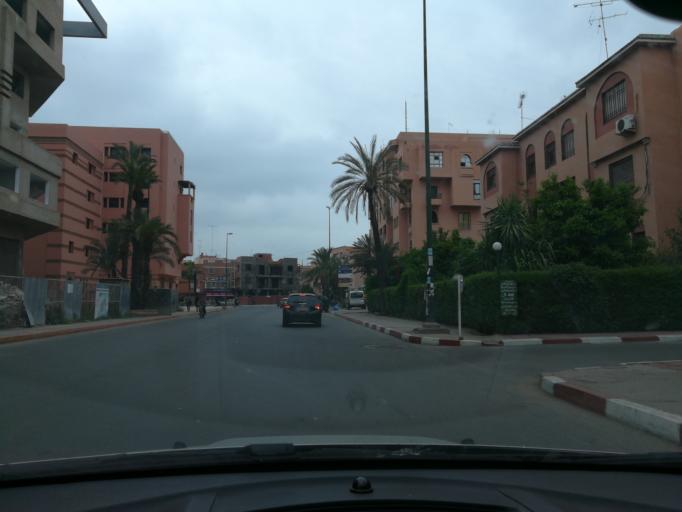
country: MA
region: Marrakech-Tensift-Al Haouz
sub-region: Marrakech
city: Marrakesh
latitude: 31.6492
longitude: -8.0020
